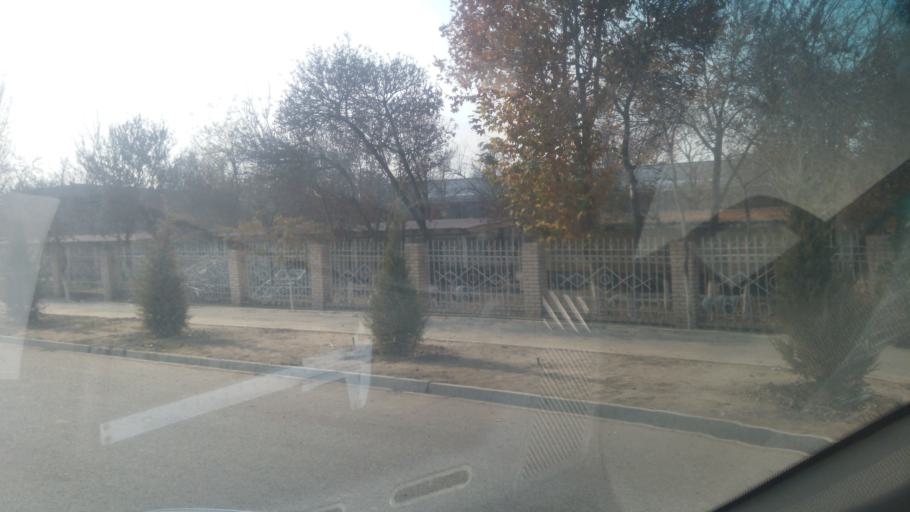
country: UZ
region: Sirdaryo
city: Guliston
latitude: 40.5132
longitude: 68.7700
